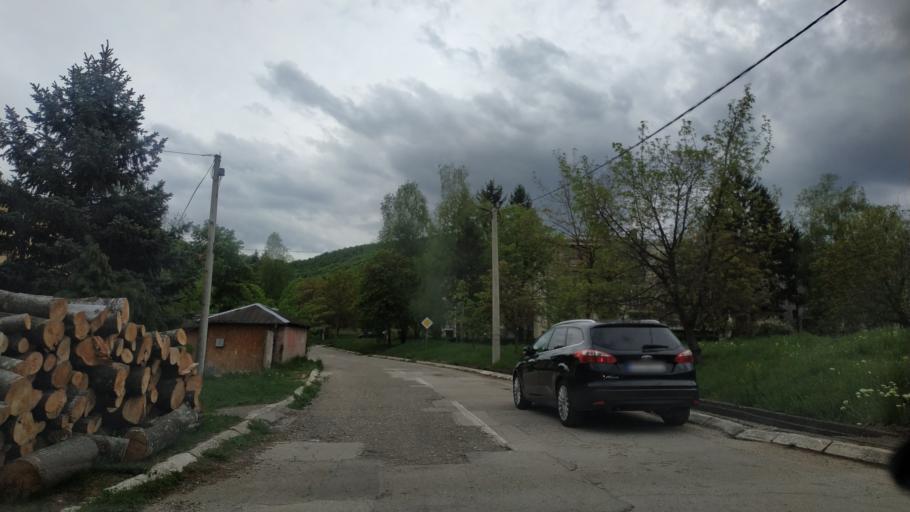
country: RS
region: Central Serbia
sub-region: Zajecarski Okrug
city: Soko Banja
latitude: 43.6415
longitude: 21.8652
